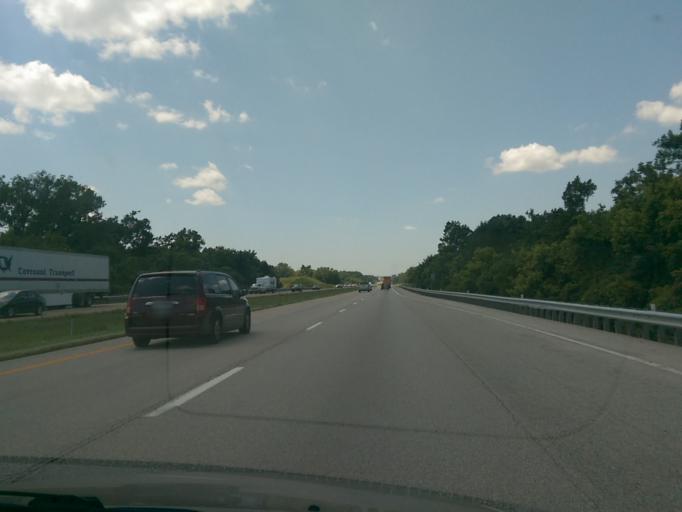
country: US
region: Missouri
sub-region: Cooper County
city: Boonville
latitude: 38.9376
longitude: -92.6966
